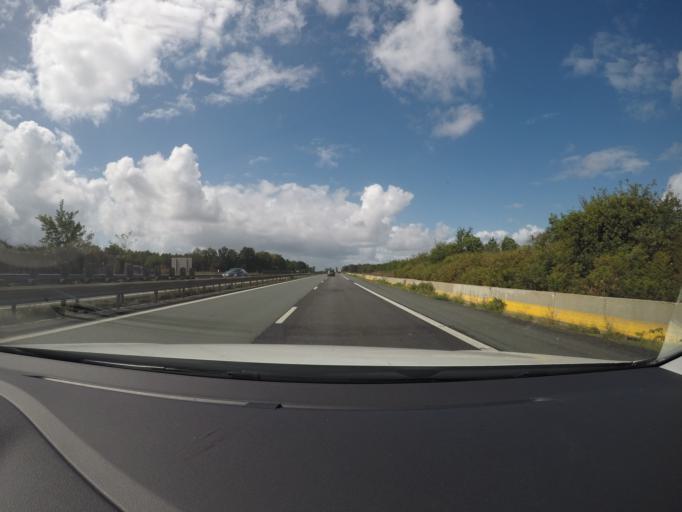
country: FR
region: Aquitaine
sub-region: Departement des Landes
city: Saint-Vincent-de-Tyrosse
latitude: 43.6827
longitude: -1.2720
